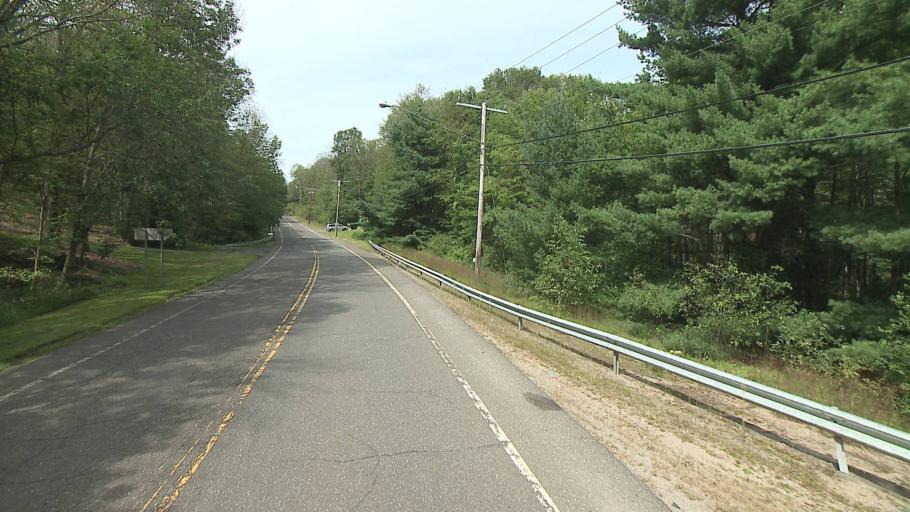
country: US
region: Connecticut
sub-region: Litchfield County
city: Oakville
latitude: 41.6154
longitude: -73.0463
